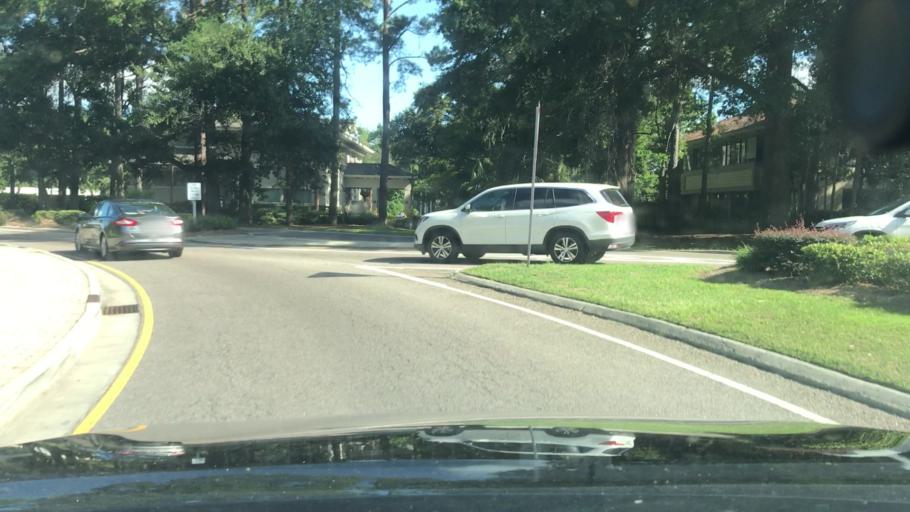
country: US
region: South Carolina
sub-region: Beaufort County
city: Hilton Head Island
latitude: 32.1557
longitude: -80.7623
